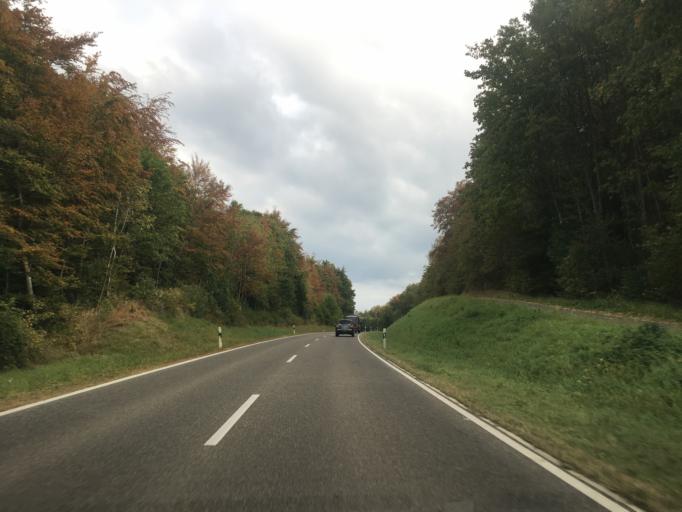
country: DE
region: Baden-Wuerttemberg
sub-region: Tuebingen Region
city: Gomadingen
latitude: 48.3723
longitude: 9.3189
